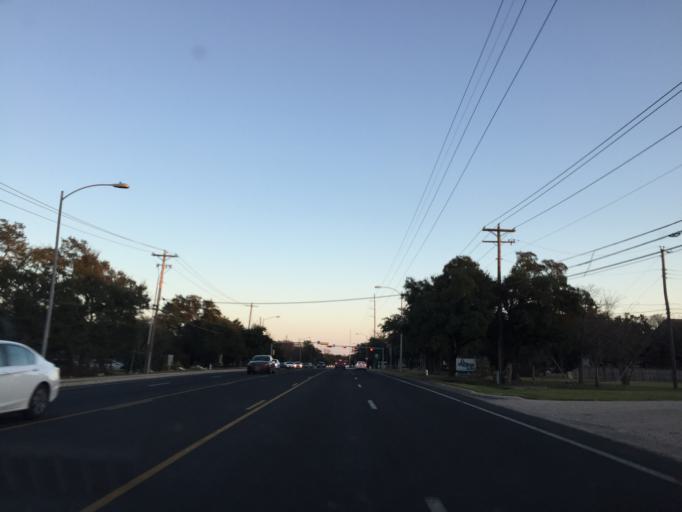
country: US
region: Texas
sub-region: Williamson County
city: Jollyville
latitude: 30.4182
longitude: -97.7512
